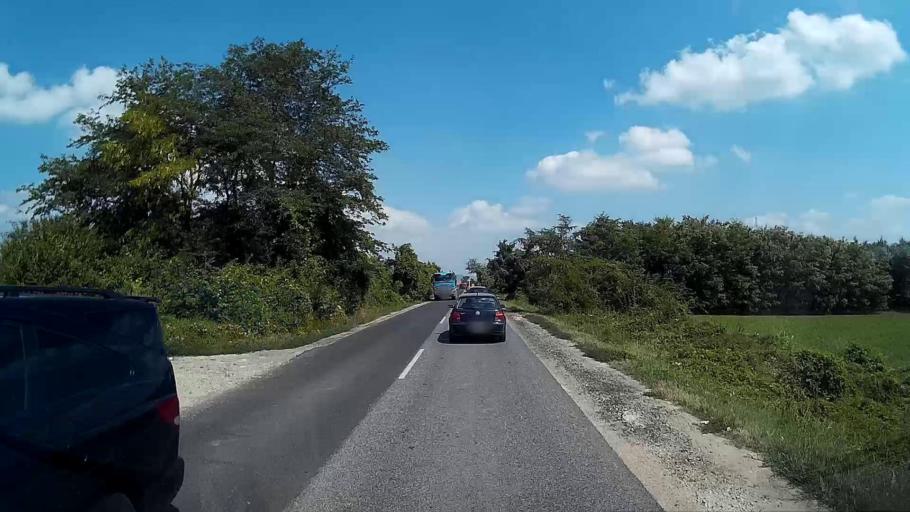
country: HU
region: Pest
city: Urom
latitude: 47.6034
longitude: 19.0215
